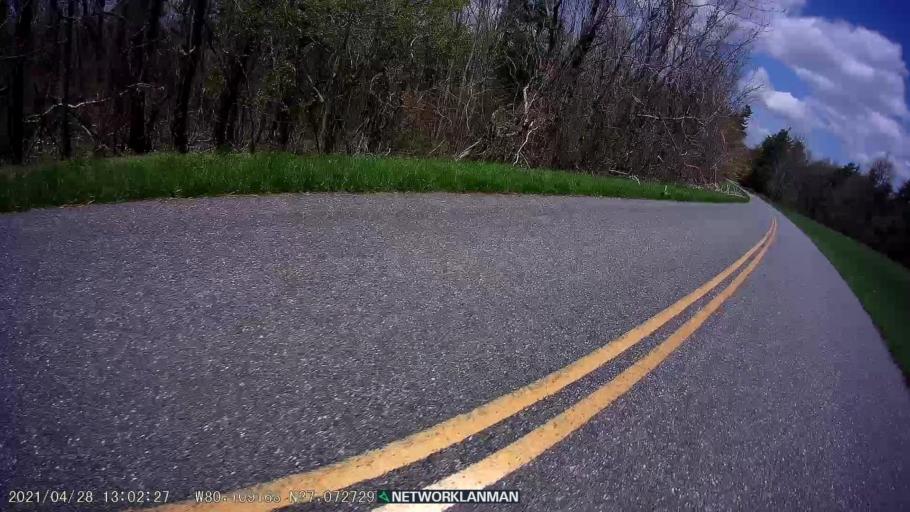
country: US
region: Virginia
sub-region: Montgomery County
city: Shawsville
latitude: 37.0731
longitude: -80.1092
